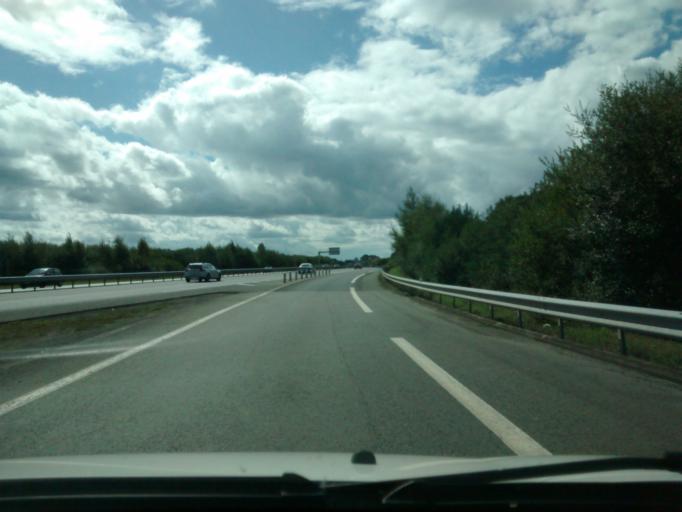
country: FR
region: Brittany
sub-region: Departement d'Ille-et-Vilaine
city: Saint-Aubin-du-Cormier
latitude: 48.2623
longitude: -1.4137
